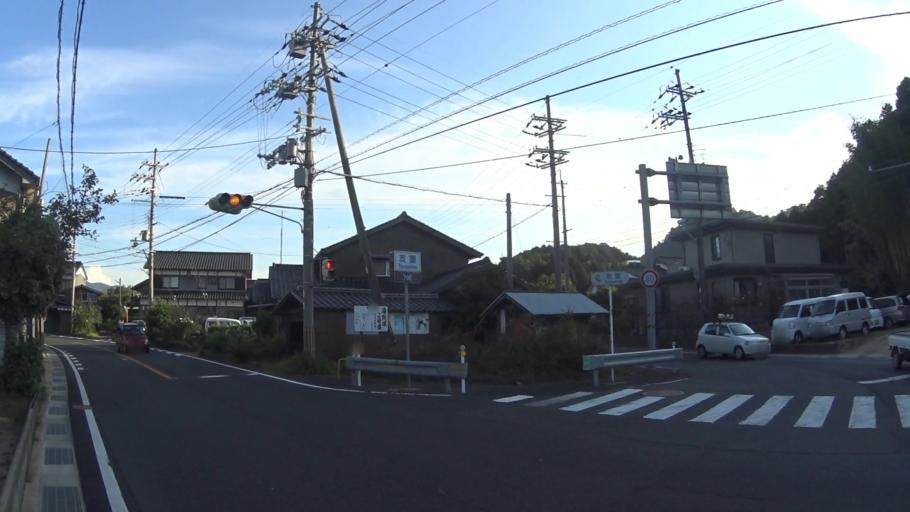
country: JP
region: Hyogo
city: Toyooka
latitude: 35.5890
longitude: 134.9247
